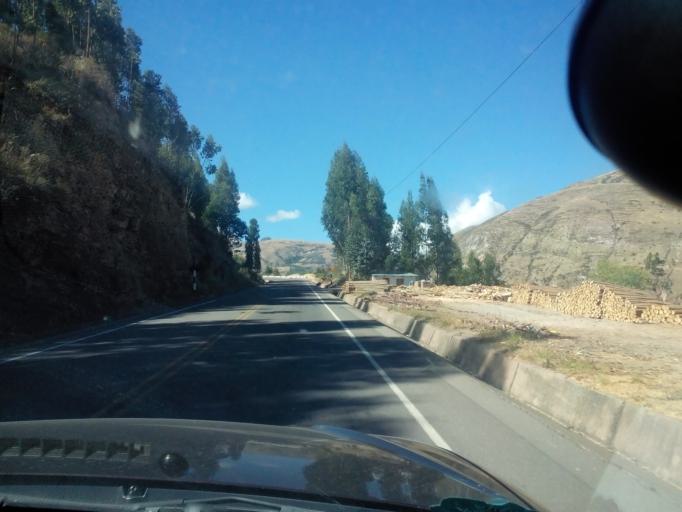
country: PE
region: Cusco
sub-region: Provincia de Quispicanchis
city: Urcos
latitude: -13.6868
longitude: -71.6109
